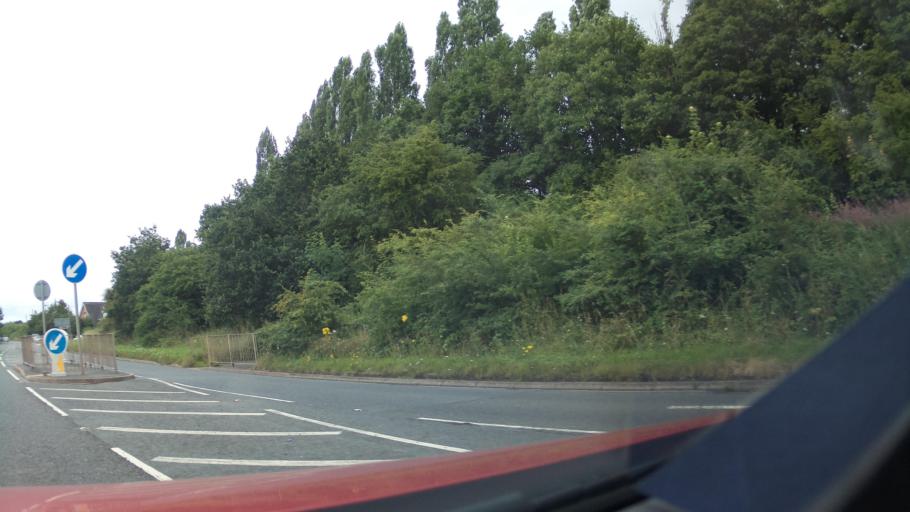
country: GB
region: England
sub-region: Worcestershire
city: Fernhill Heath
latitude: 52.2294
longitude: -2.1696
